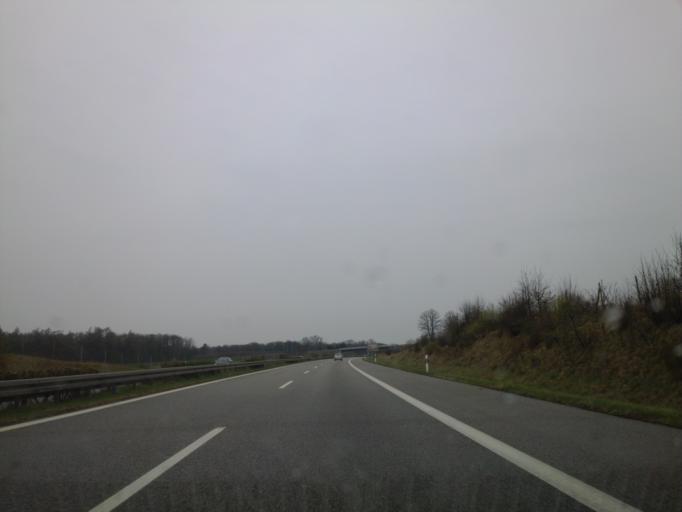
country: DE
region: Mecklenburg-Vorpommern
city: Tessin
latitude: 54.0089
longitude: 12.5355
